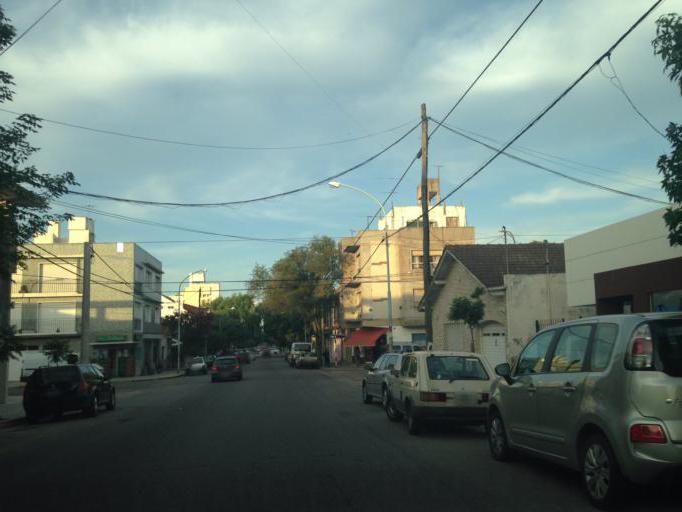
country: AR
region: Buenos Aires
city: Mar del Plata
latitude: -38.0149
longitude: -57.5508
